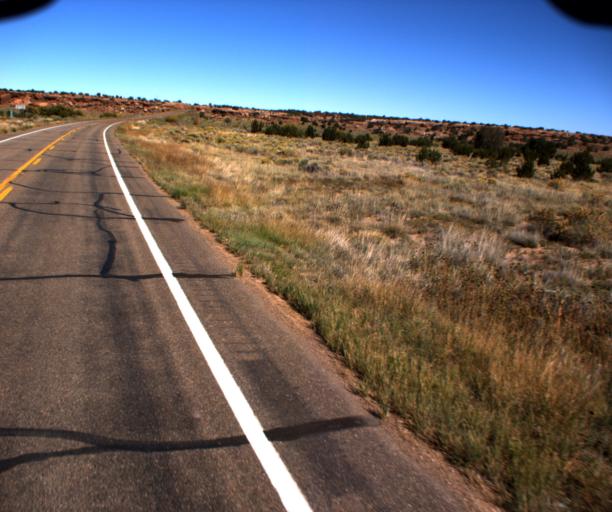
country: US
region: Arizona
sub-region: Apache County
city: Saint Johns
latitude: 34.4467
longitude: -109.4103
